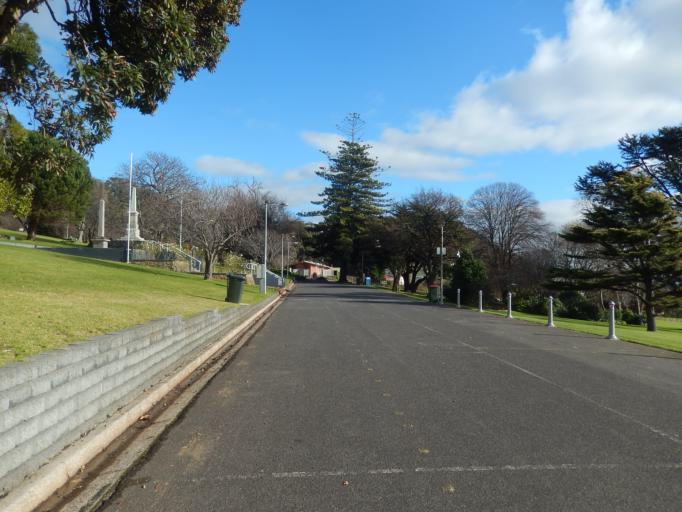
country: AU
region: Tasmania
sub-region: Burnie
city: Burnie
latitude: -41.0472
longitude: 145.8976
